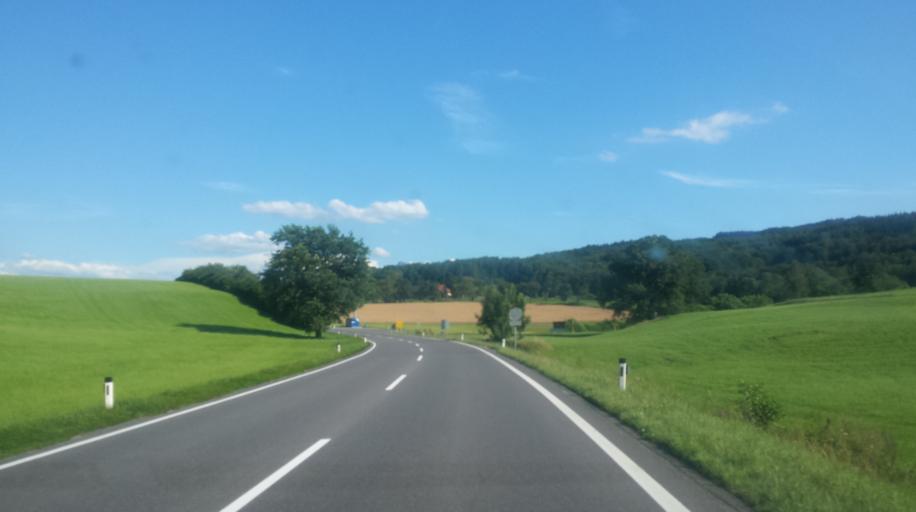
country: AT
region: Upper Austria
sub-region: Politischer Bezirk Vocklabruck
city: Aurach am Hongar
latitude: 47.9581
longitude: 13.7184
